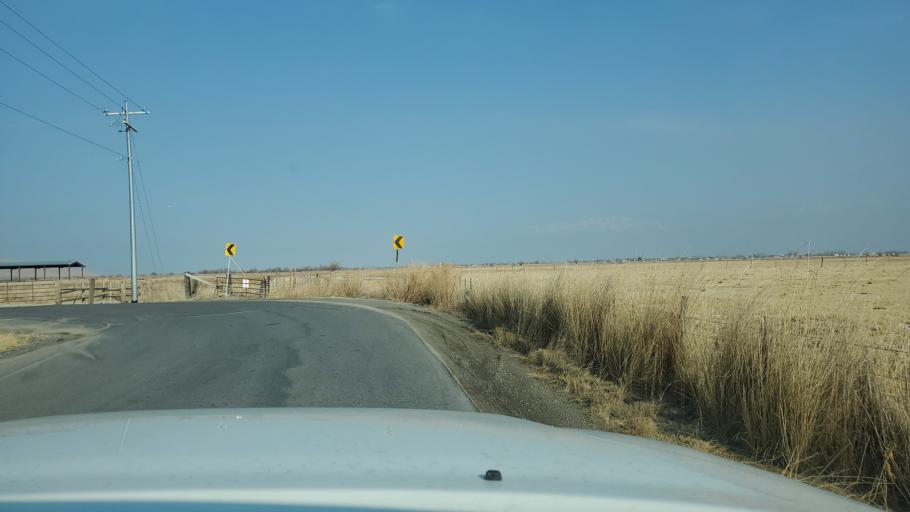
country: US
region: Utah
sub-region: Utah County
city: West Mountain
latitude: 40.0994
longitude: -111.7880
